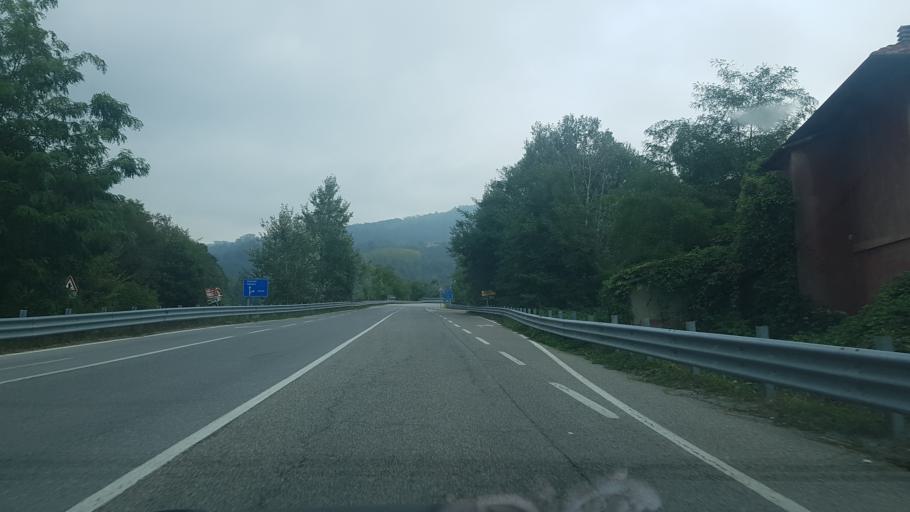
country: IT
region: Piedmont
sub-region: Provincia di Cuneo
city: Rocca Ciglie
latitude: 44.4259
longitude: 7.9522
